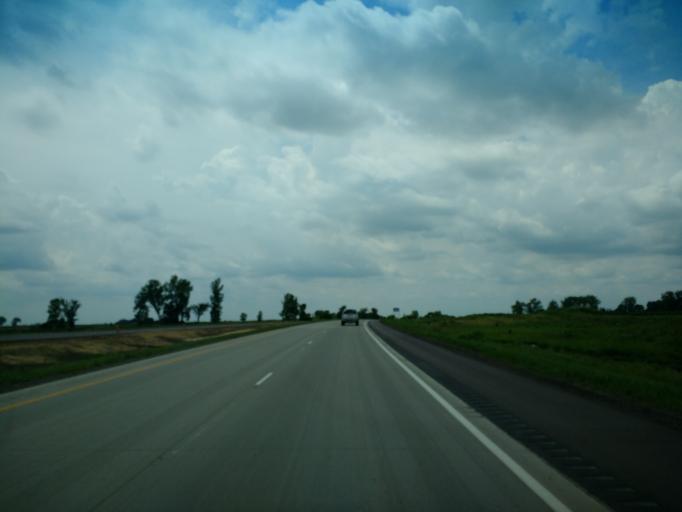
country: US
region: Minnesota
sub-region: Cottonwood County
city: Windom
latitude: 43.9035
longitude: -95.0616
